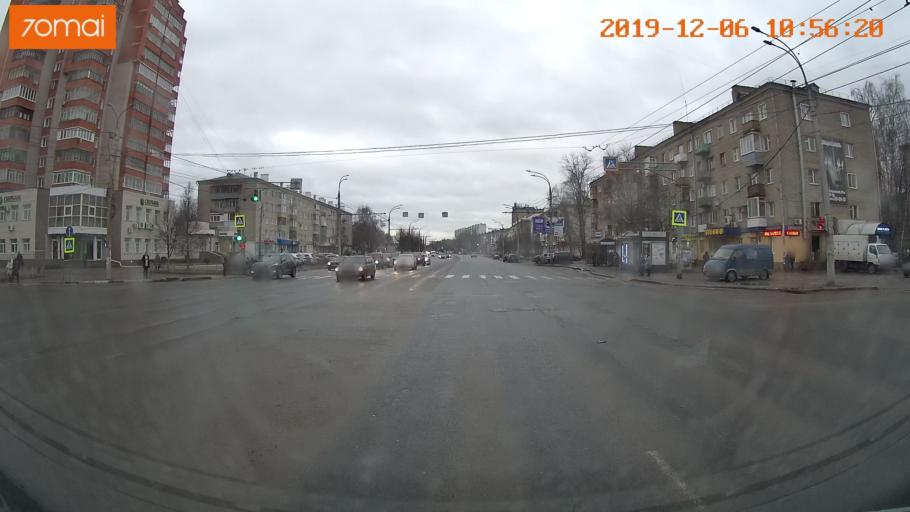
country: RU
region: Ivanovo
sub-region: Gorod Ivanovo
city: Ivanovo
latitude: 56.9717
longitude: 40.9738
